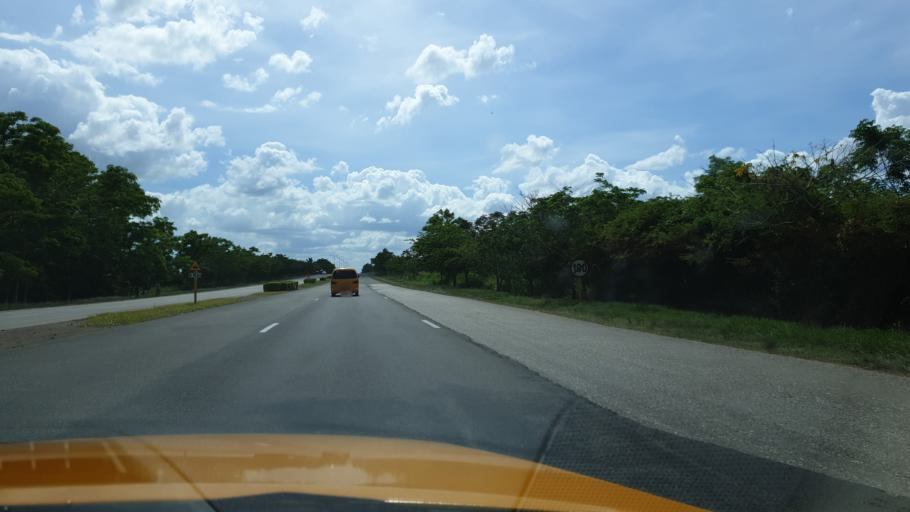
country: CU
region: Cienfuegos
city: Cruces
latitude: 22.4525
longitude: -80.2872
